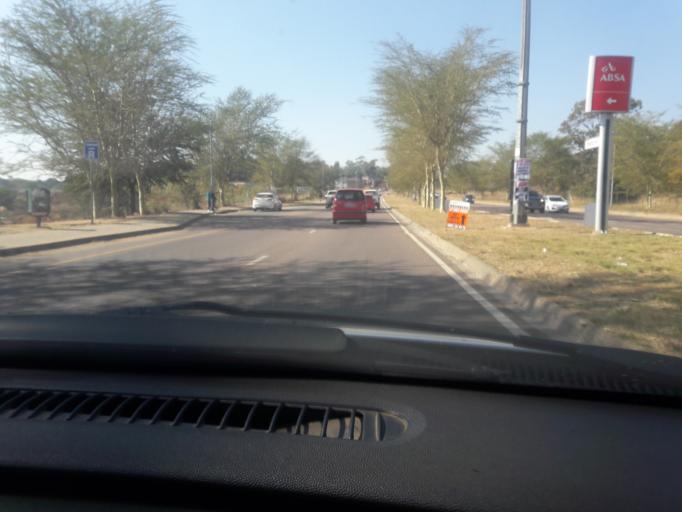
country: ZA
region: Gauteng
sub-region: City of Tshwane Metropolitan Municipality
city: Pretoria
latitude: -25.7684
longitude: 28.3272
